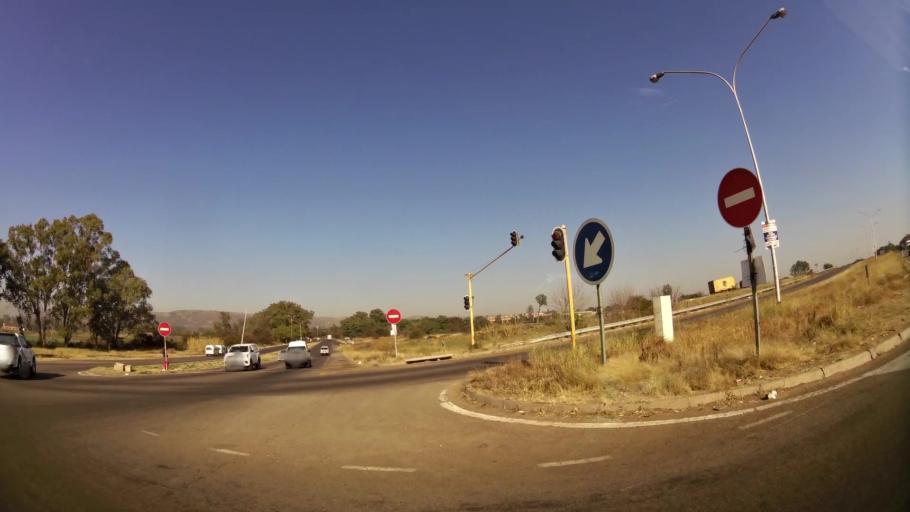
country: ZA
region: Gauteng
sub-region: City of Tshwane Metropolitan Municipality
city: Pretoria
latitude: -25.6586
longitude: 28.1866
